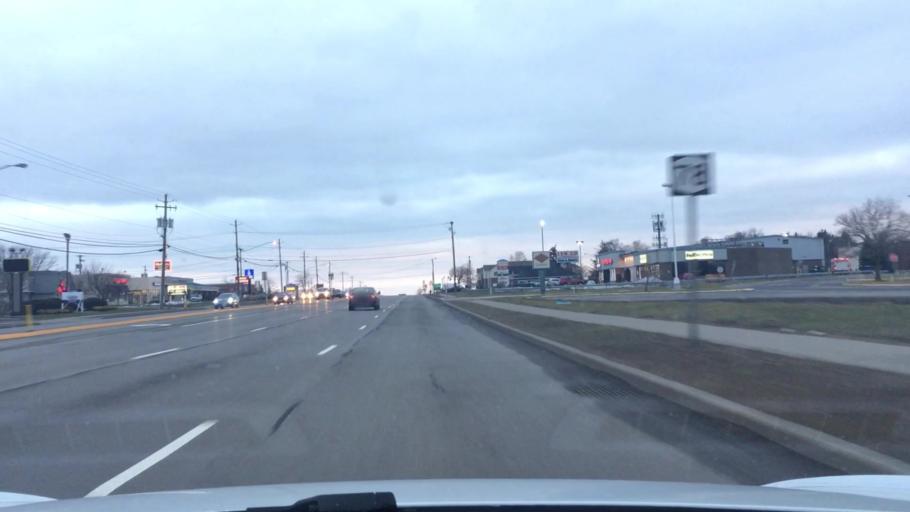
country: US
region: New York
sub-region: Erie County
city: Harris Hill
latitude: 42.9736
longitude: -78.6967
